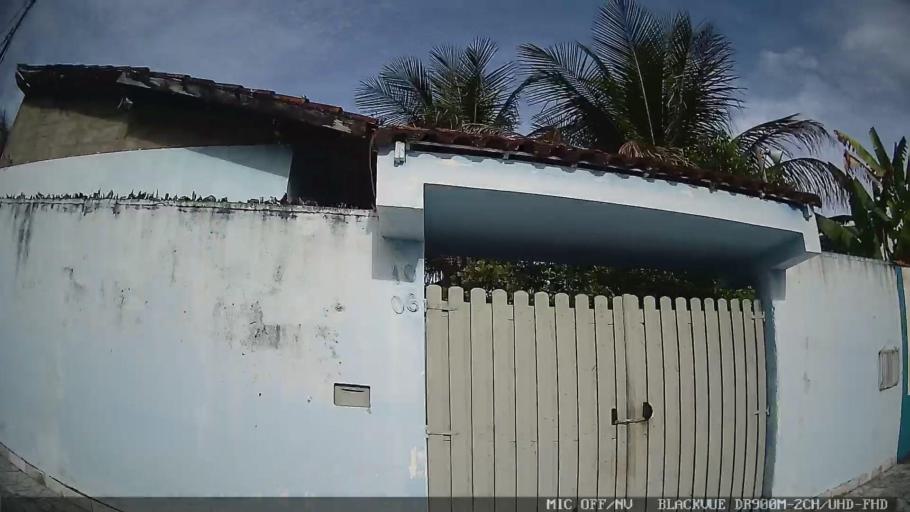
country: BR
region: Sao Paulo
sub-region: Itanhaem
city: Itanhaem
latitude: -24.1621
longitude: -46.7636
